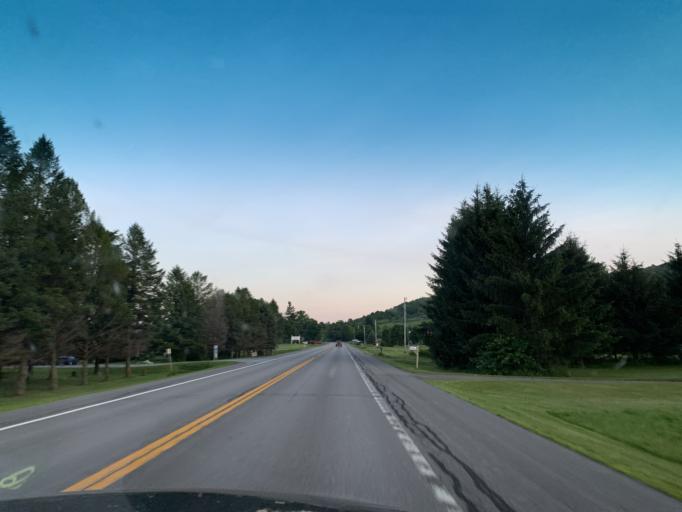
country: US
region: New York
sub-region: Oneida County
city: Waterville
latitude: 42.8369
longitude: -75.2554
